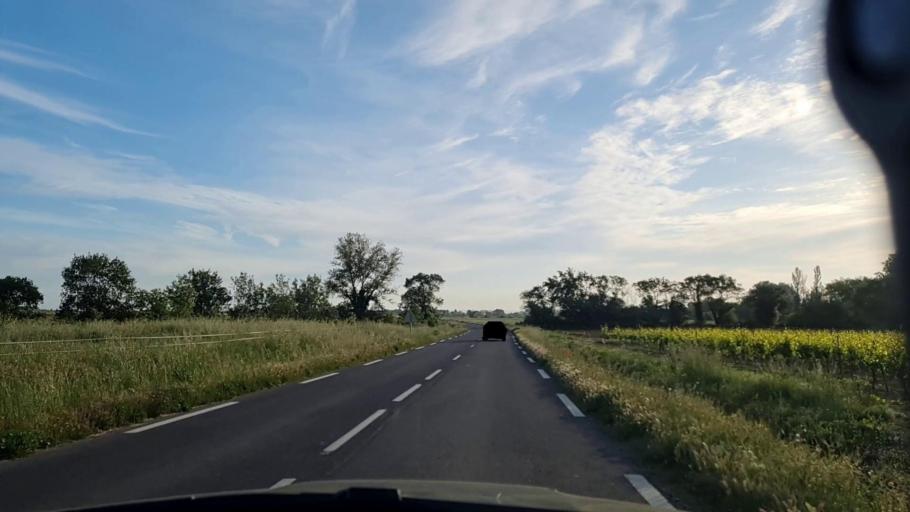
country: FR
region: Languedoc-Roussillon
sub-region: Departement du Gard
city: Saint-Mamert-du-Gard
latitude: 43.8930
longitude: 4.1975
